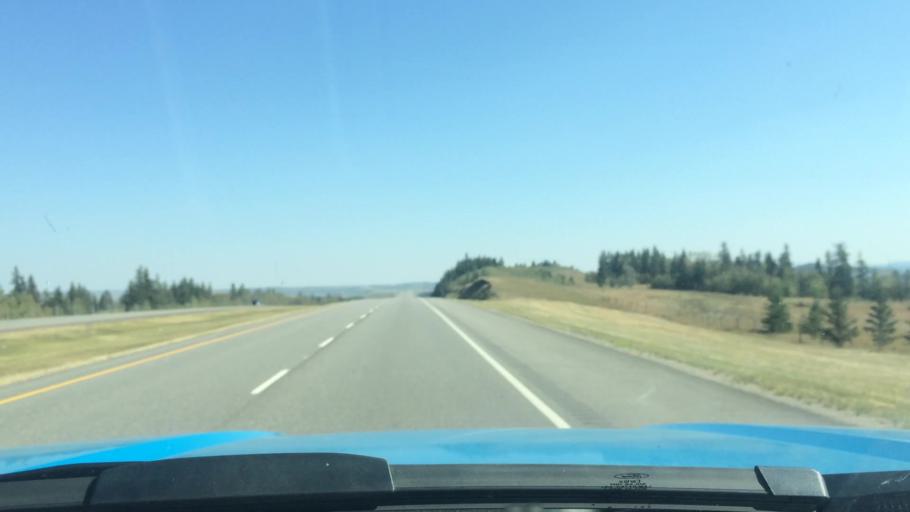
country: CA
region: Alberta
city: Cochrane
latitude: 51.1397
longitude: -114.7160
